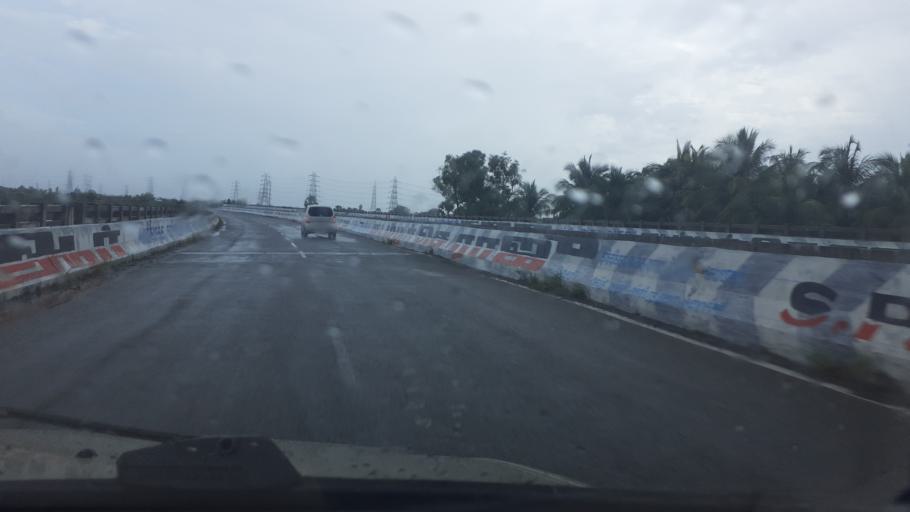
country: IN
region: Tamil Nadu
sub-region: Thoothukkudi
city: Kayattar
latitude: 8.9400
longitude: 77.7655
